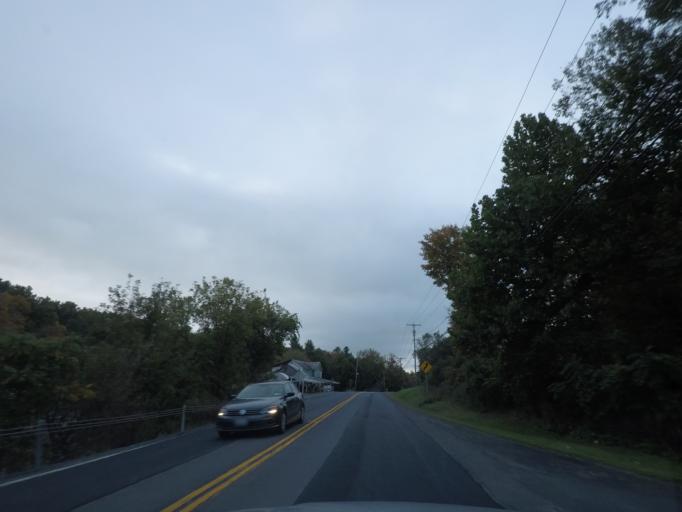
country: US
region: New York
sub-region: Rensselaer County
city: Nassau
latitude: 42.5620
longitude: -73.6402
